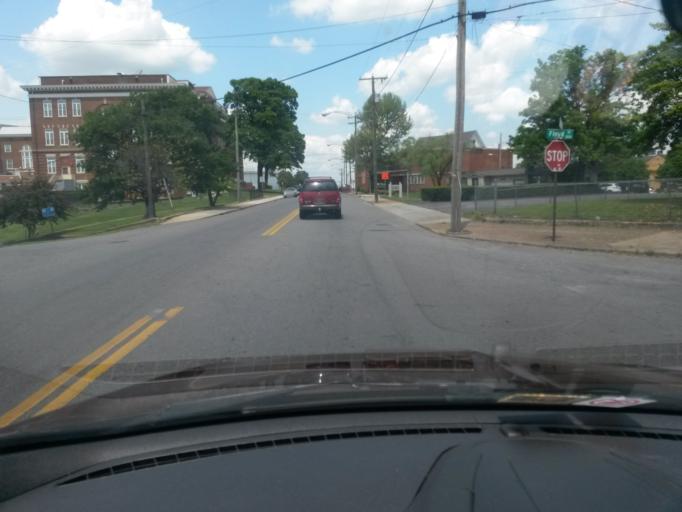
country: US
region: Virginia
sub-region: City of Lynchburg
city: Lynchburg
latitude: 37.4092
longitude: -79.1537
